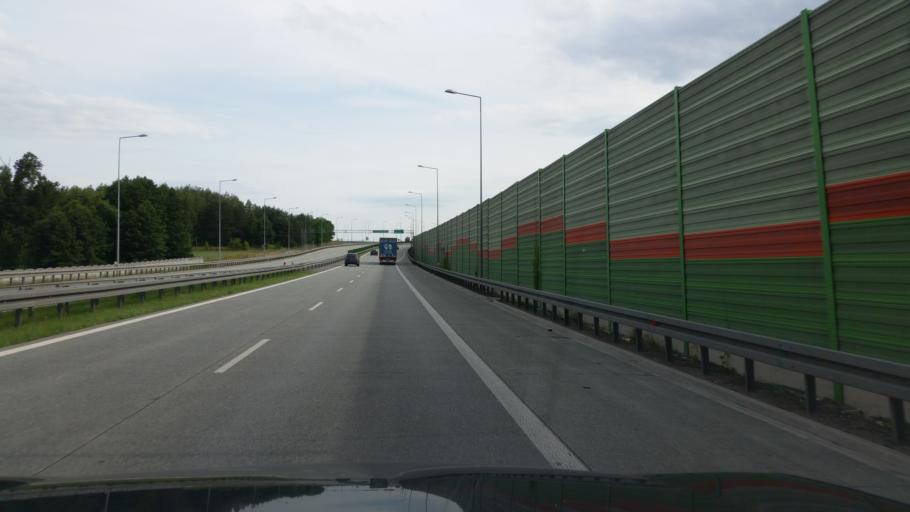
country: PL
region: Lodz Voivodeship
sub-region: Powiat rawski
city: Rawa Mazowiecka
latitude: 51.7088
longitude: 20.2193
